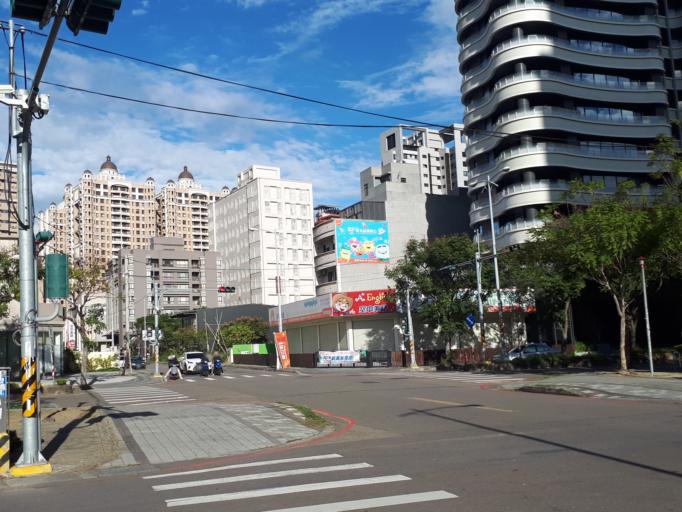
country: TW
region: Taiwan
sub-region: Hsinchu
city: Zhubei
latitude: 24.8049
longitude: 121.0334
